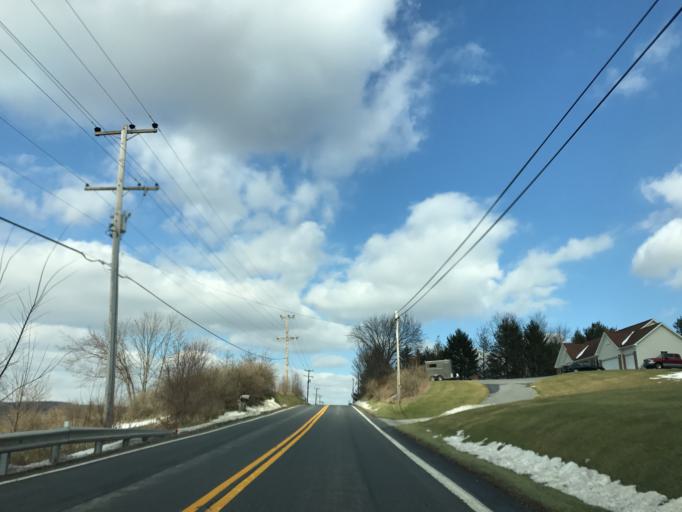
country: US
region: Maryland
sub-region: Carroll County
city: Manchester
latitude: 39.6652
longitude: -76.9443
